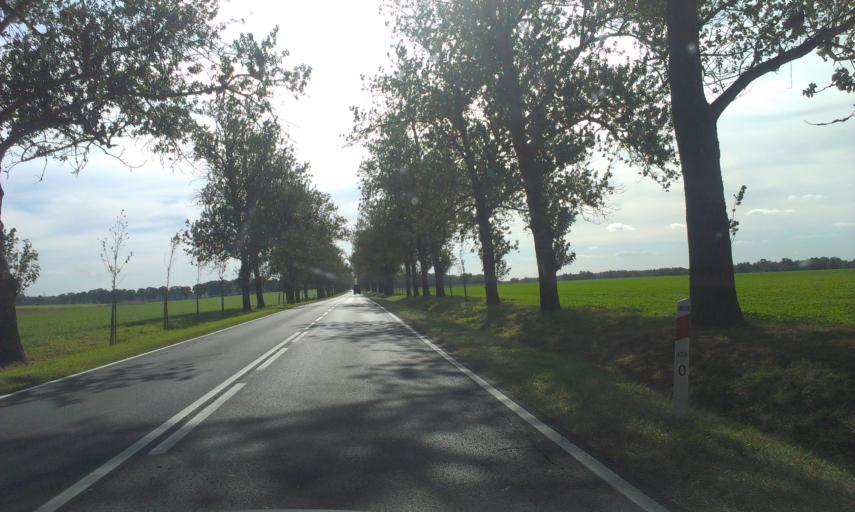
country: PL
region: Greater Poland Voivodeship
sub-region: Powiat zlotowski
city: Okonek
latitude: 53.5981
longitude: 16.8130
